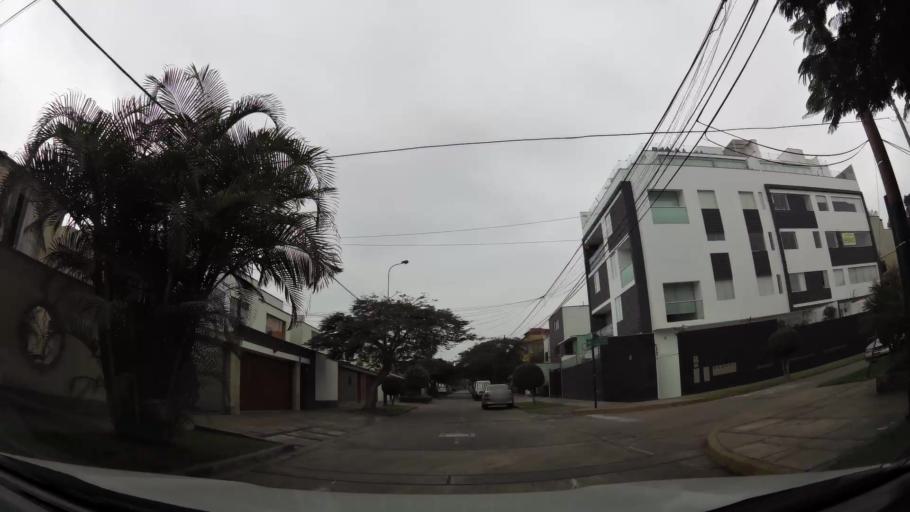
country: PE
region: Lima
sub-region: Lima
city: Surco
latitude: -12.1205
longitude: -76.9909
